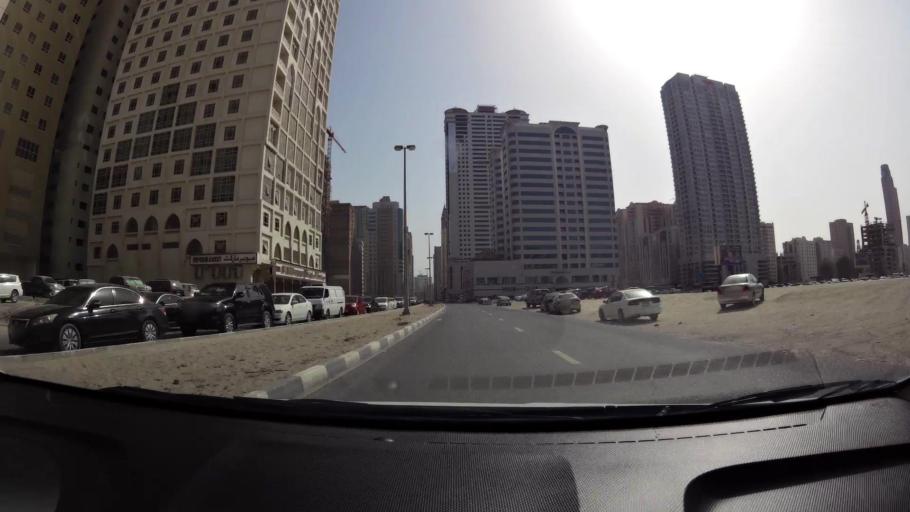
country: AE
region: Ash Shariqah
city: Sharjah
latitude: 25.3075
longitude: 55.3740
